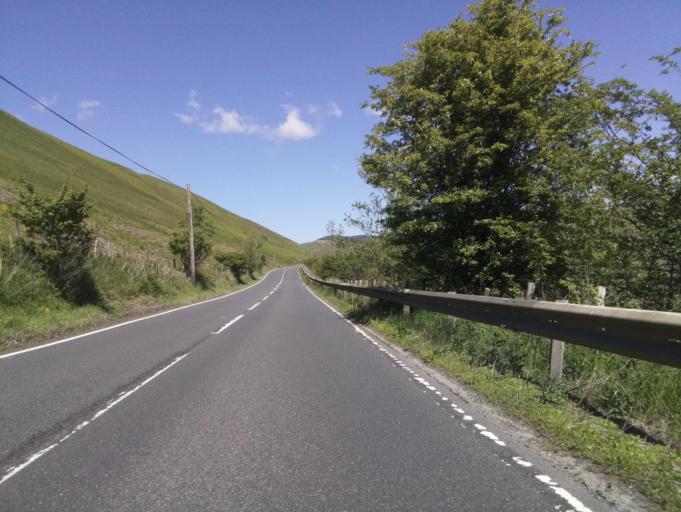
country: GB
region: Scotland
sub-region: Dumfries and Galloway
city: Langholm
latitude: 55.2356
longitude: -2.9752
